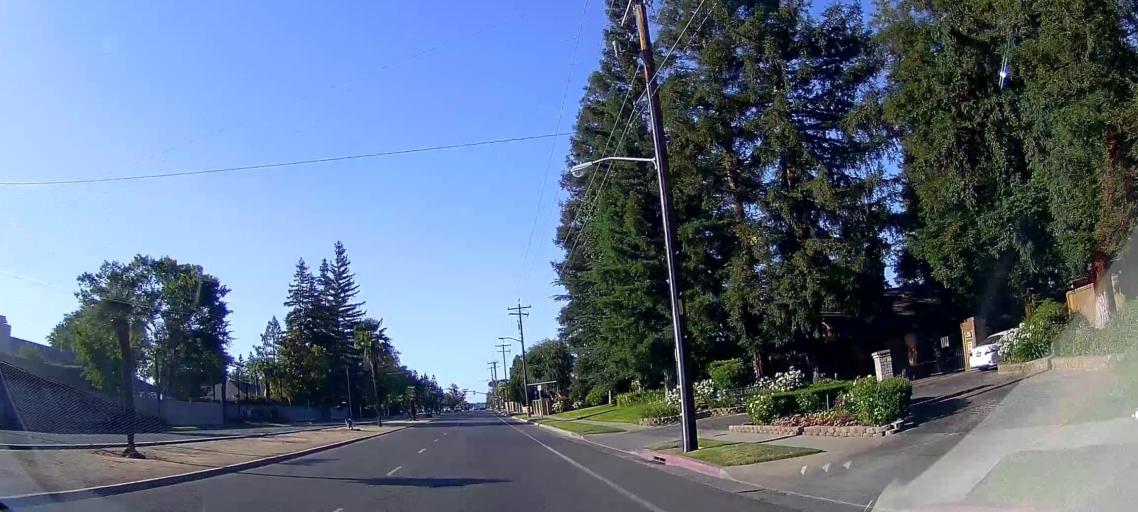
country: US
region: California
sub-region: Fresno County
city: Fresno
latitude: 36.8282
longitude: -119.8082
